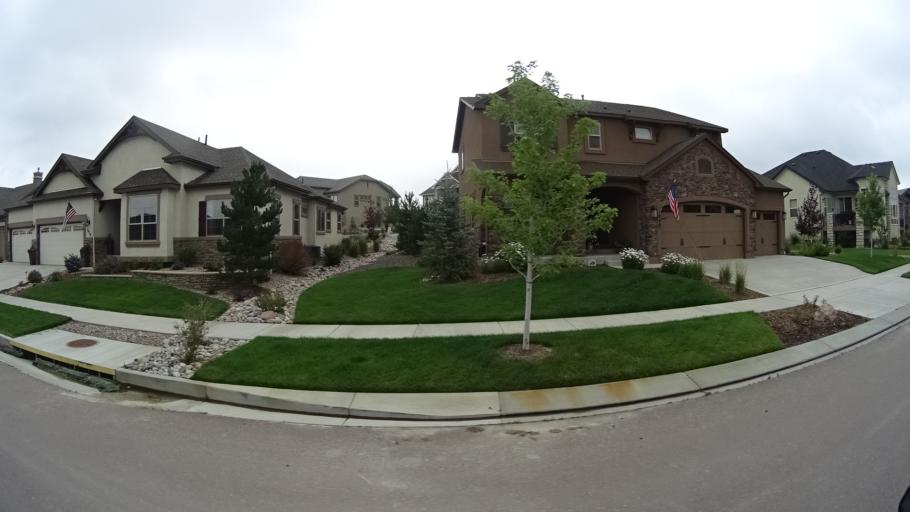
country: US
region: Colorado
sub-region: El Paso County
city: Gleneagle
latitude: 39.0275
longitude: -104.7939
